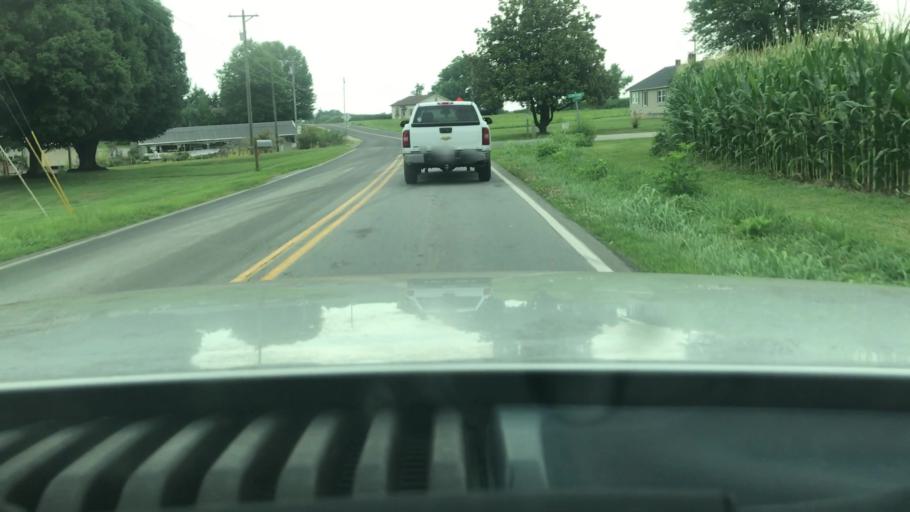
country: US
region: North Carolina
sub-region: Surry County
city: Dobson
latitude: 36.3971
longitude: -80.7967
